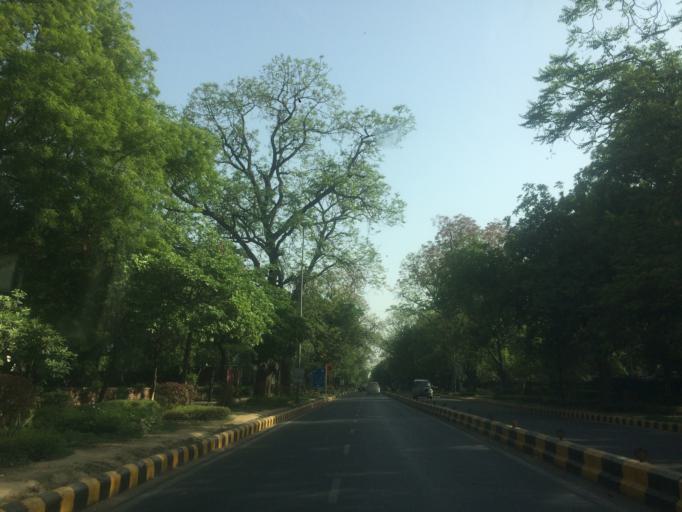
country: IN
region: NCT
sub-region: New Delhi
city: New Delhi
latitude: 28.6177
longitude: 77.2314
